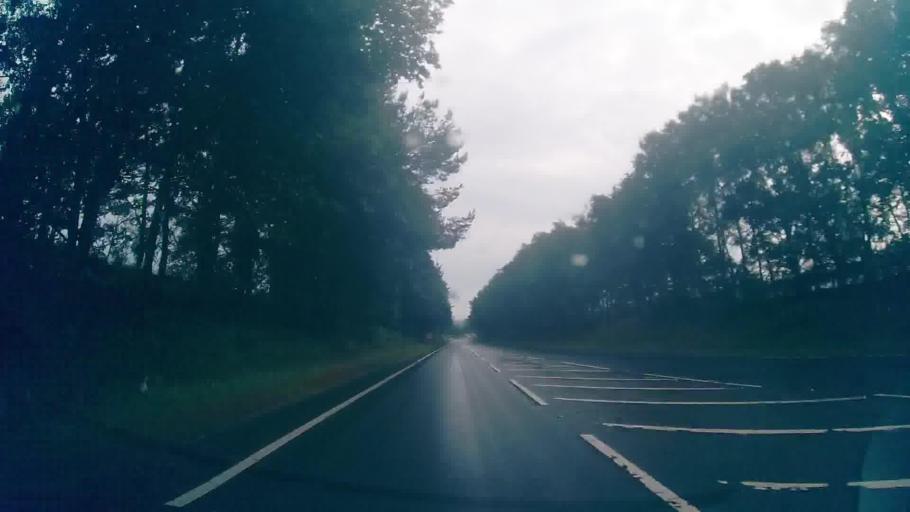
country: GB
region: Scotland
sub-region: Dumfries and Galloway
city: Locharbriggs
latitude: 55.0660
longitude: -3.5123
